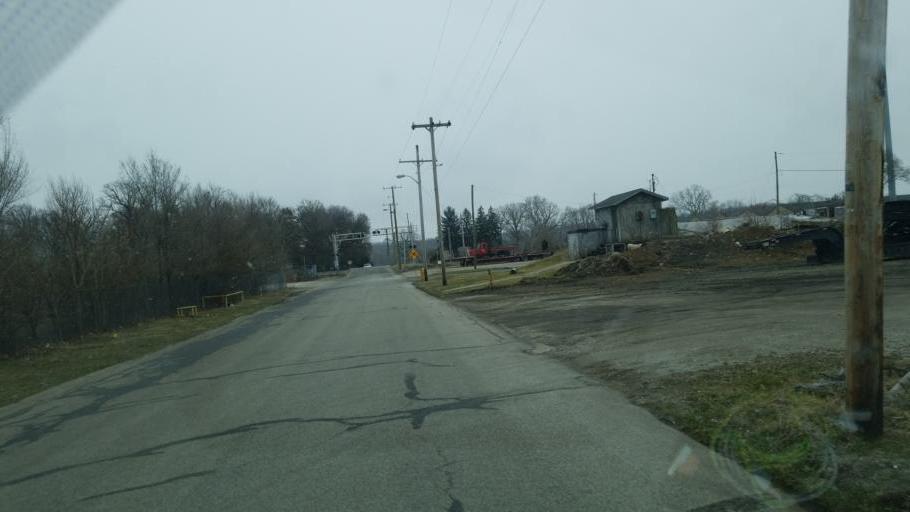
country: US
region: Indiana
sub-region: Wabash County
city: Wabash
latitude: 40.8015
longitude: -85.8425
